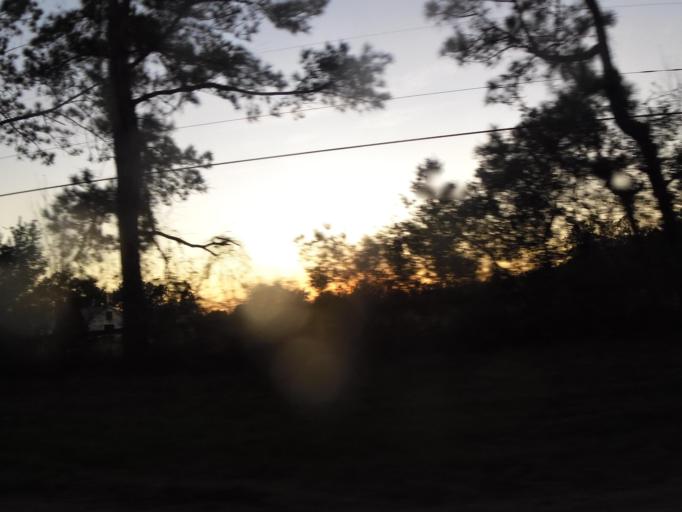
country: US
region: Florida
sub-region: Clay County
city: Asbury Lake
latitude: 29.9693
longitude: -81.7940
